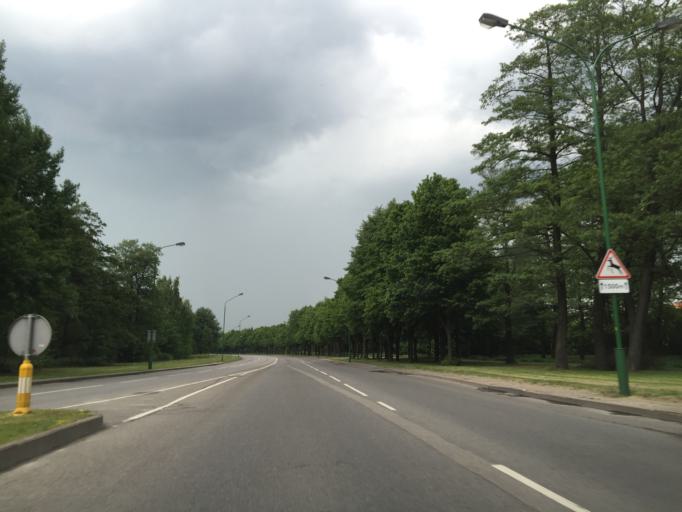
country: LT
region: Klaipedos apskritis
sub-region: Klaipeda
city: Klaipeda
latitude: 55.7341
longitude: 21.1287
